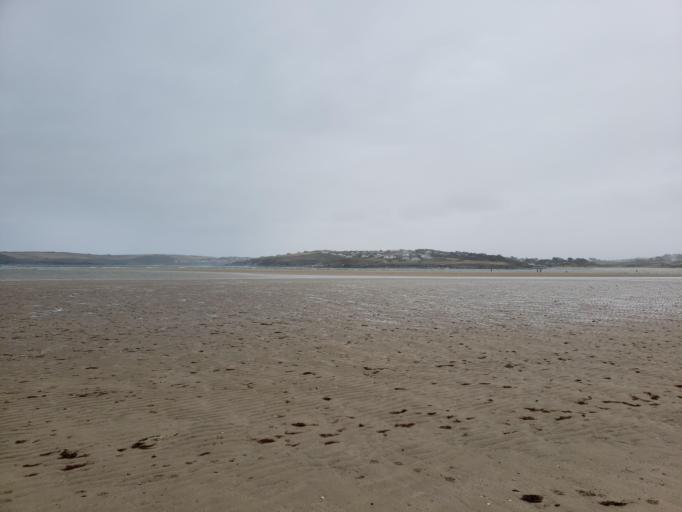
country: GB
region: England
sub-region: Cornwall
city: Padstow
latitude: 50.5599
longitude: -4.9470
